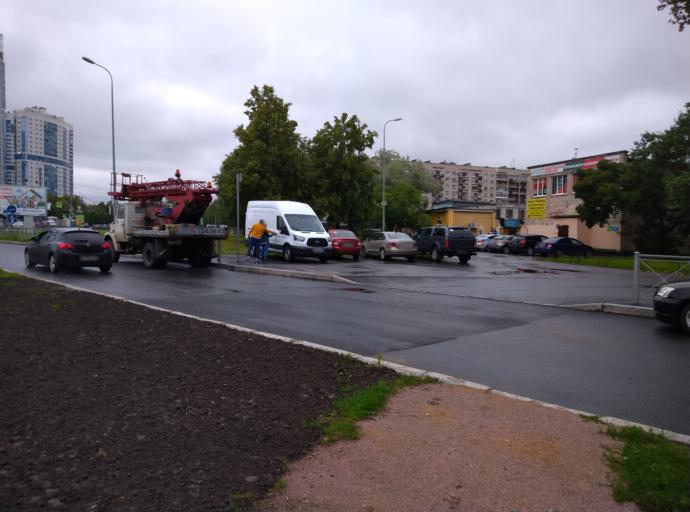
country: RU
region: St.-Petersburg
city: Kupchino
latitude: 59.8515
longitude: 30.3535
